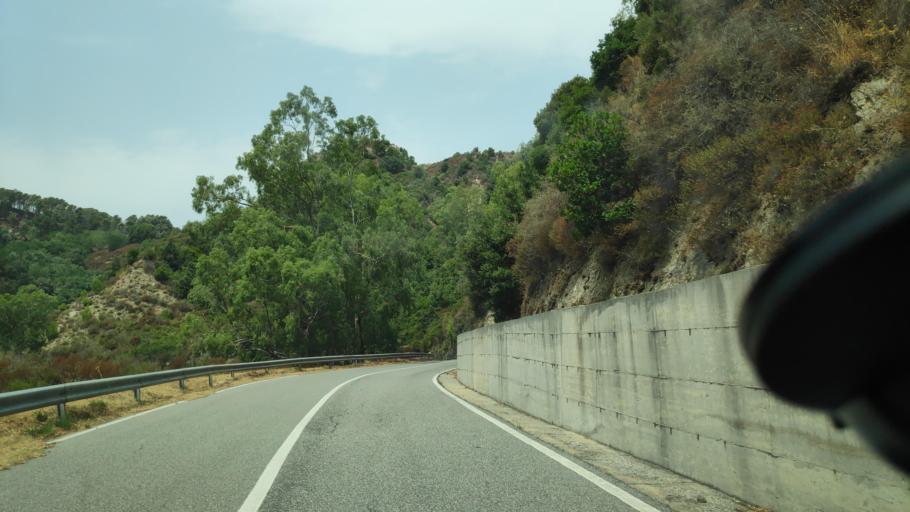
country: IT
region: Calabria
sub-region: Provincia di Catanzaro
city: San Sostene
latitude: 38.6403
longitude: 16.5108
